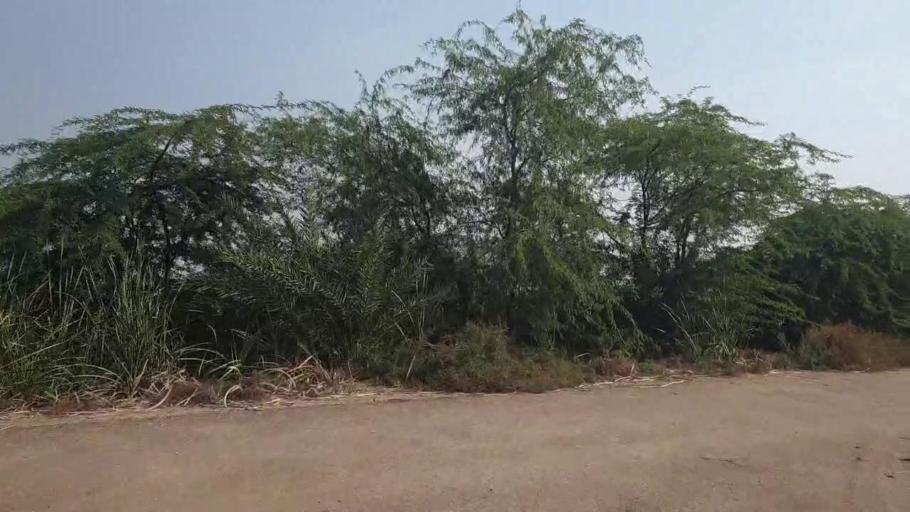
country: PK
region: Sindh
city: Jamshoro
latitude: 25.4593
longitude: 68.3366
